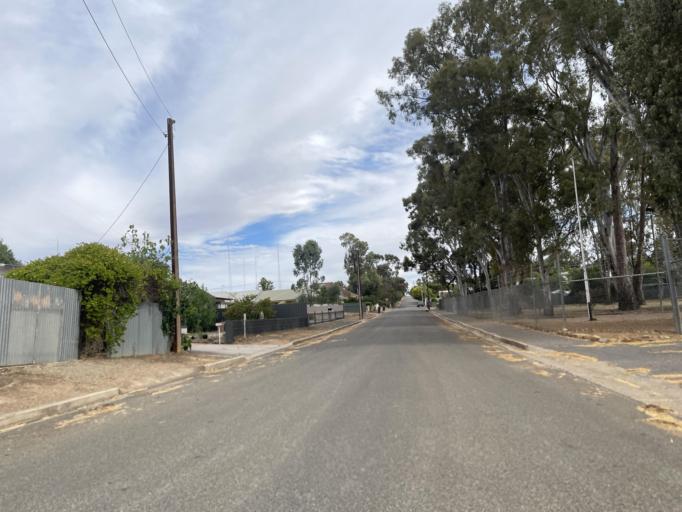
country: AU
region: South Australia
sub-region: Clare and Gilbert Valleys
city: Clare
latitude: -33.8396
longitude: 138.6146
